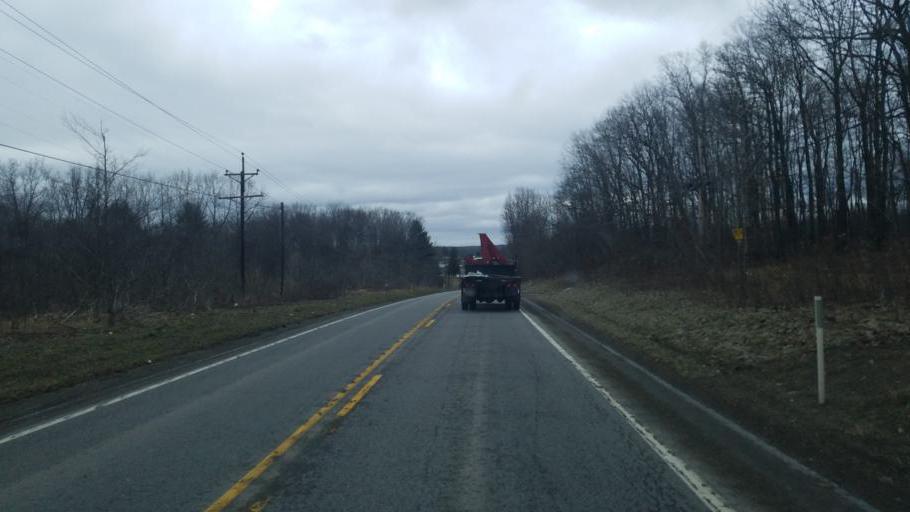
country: US
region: Pennsylvania
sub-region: Clarion County
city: Marianne
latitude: 41.3649
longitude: -79.3149
